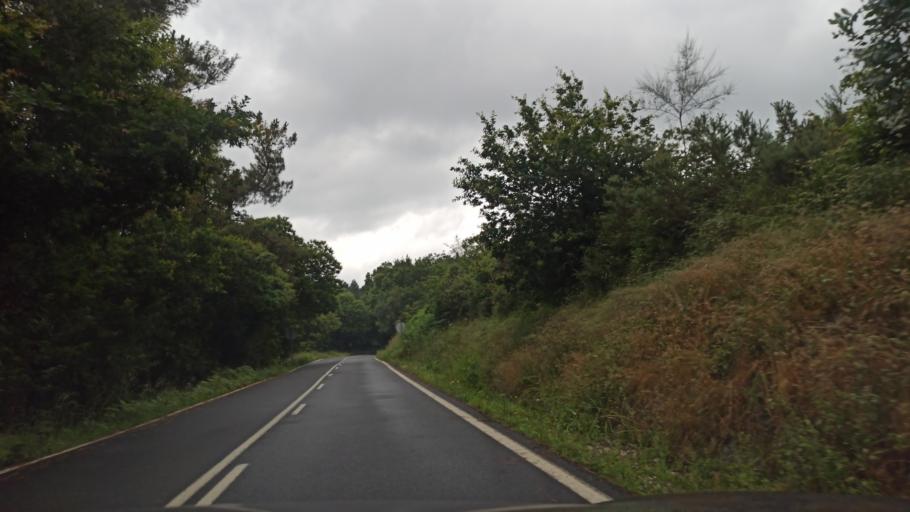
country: ES
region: Galicia
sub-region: Provincia da Coruna
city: Santiso
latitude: 42.7815
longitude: -8.0813
